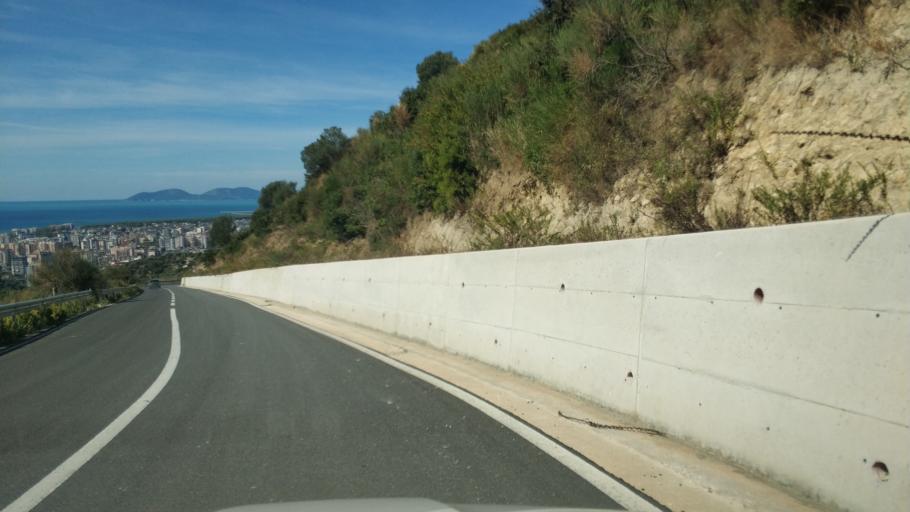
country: AL
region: Vlore
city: Vlore
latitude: 40.4568
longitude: 19.5130
